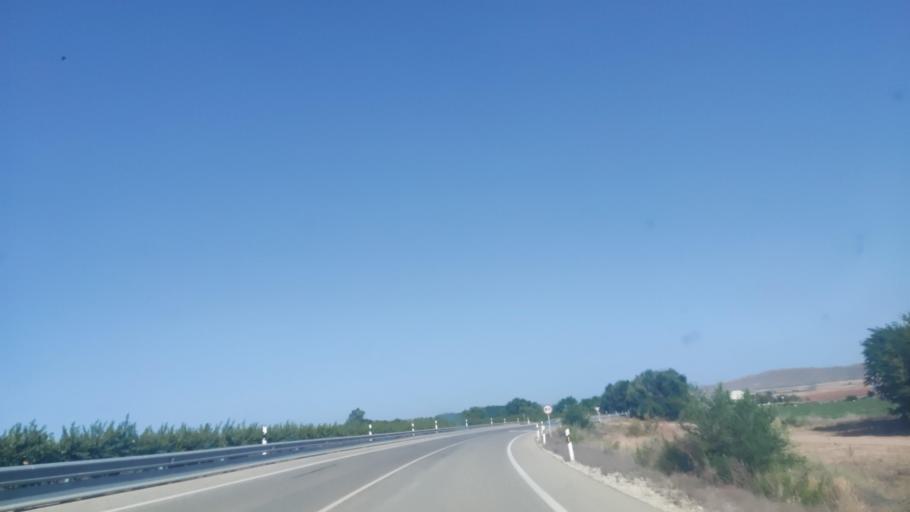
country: ES
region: Castille-La Mancha
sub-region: Provincia de Albacete
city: Hellin
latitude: 38.4924
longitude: -1.6383
